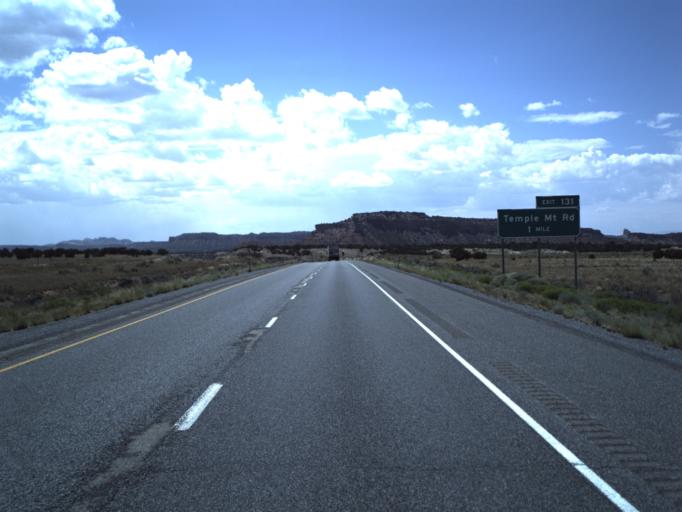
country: US
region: Utah
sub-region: Emery County
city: Castle Dale
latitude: 38.8918
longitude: -110.6373
